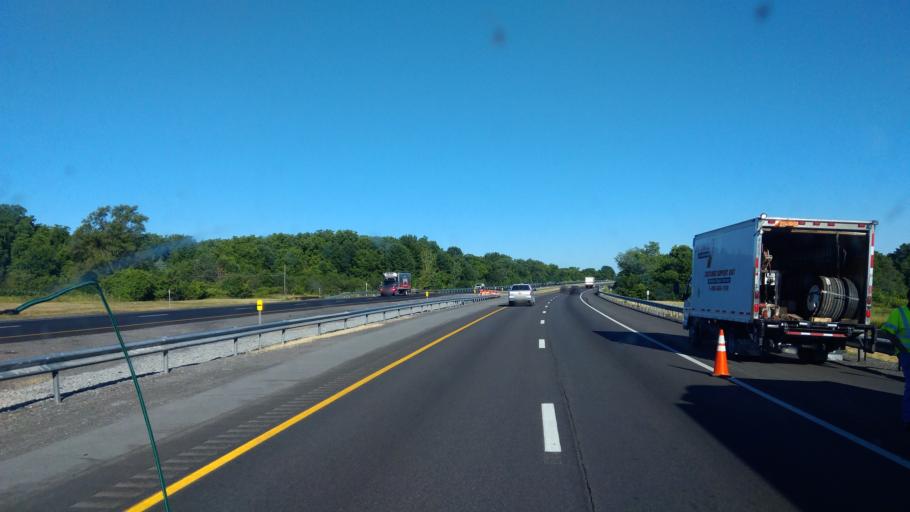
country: US
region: New York
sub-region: Ontario County
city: Phelps
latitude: 42.9696
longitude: -77.0741
